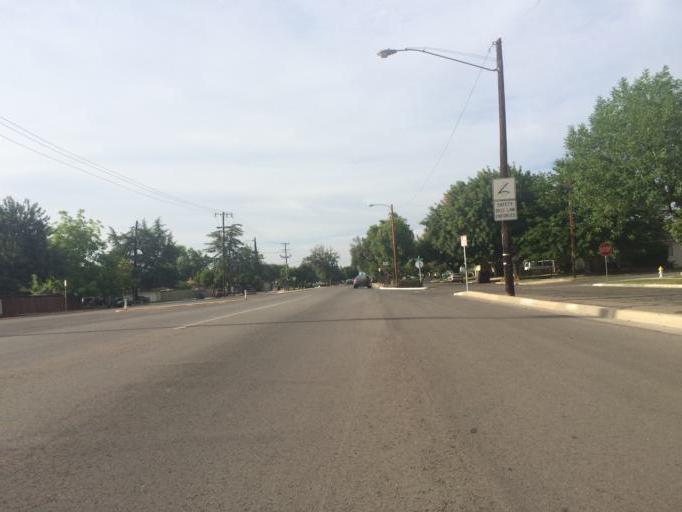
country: US
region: California
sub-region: Fresno County
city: Fresno
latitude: 36.7953
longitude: -119.7722
